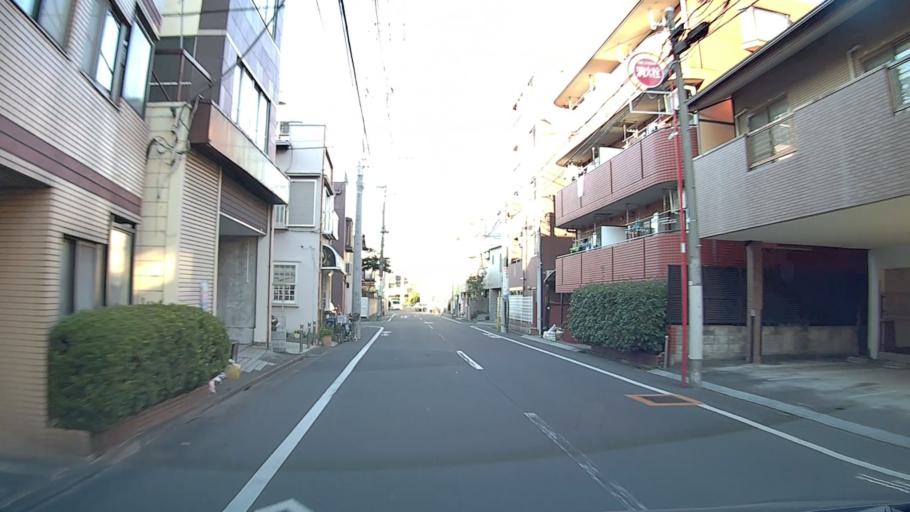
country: JP
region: Tokyo
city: Tokyo
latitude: 35.7261
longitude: 139.6626
